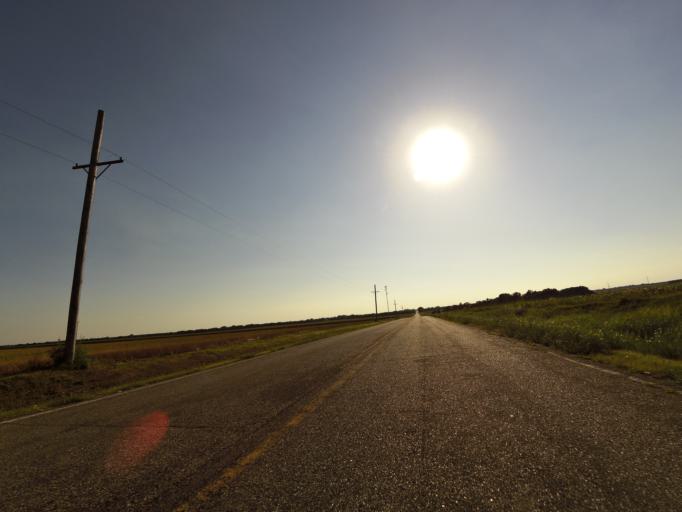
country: US
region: Kansas
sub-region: McPherson County
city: Moundridge
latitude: 38.1451
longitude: -97.5718
